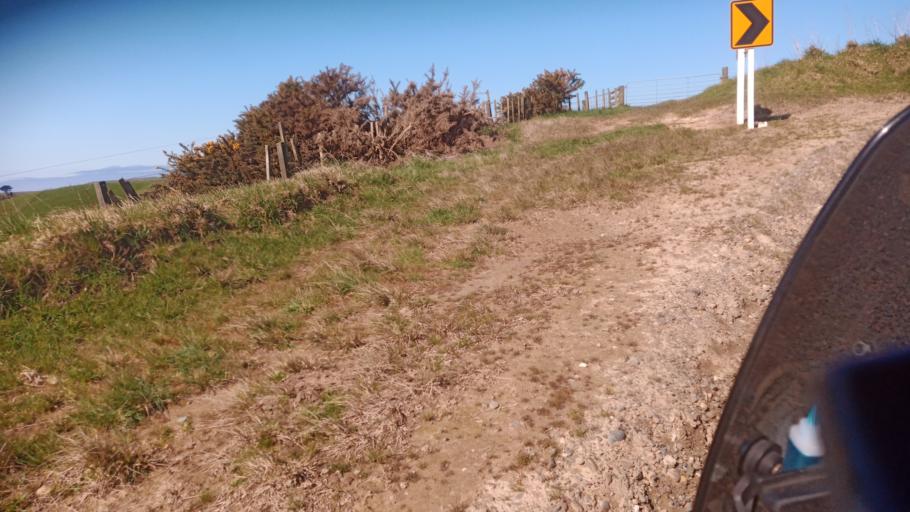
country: NZ
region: Gisborne
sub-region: Gisborne District
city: Gisborne
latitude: -39.1155
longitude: 177.9635
